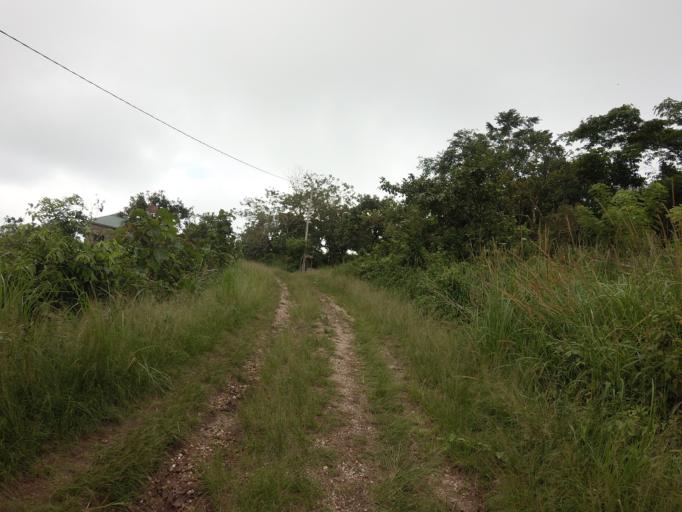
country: GH
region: Volta
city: Kpandu
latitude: 6.8525
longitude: 0.4339
